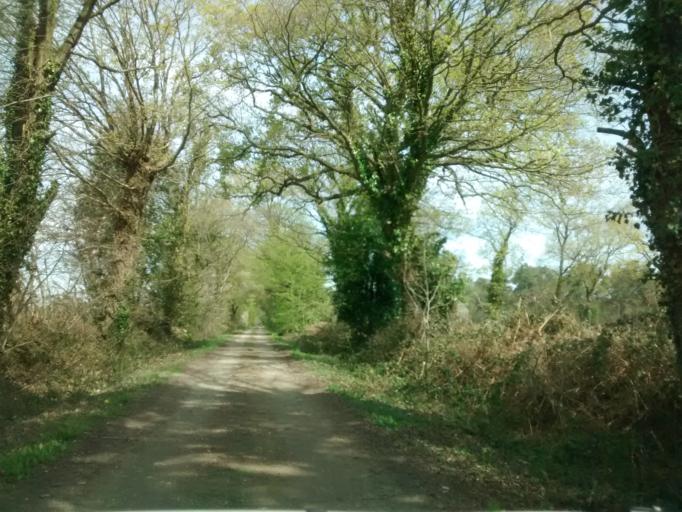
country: FR
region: Brittany
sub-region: Departement d'Ille-et-Vilaine
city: Fouillard
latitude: 48.1660
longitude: -1.5966
